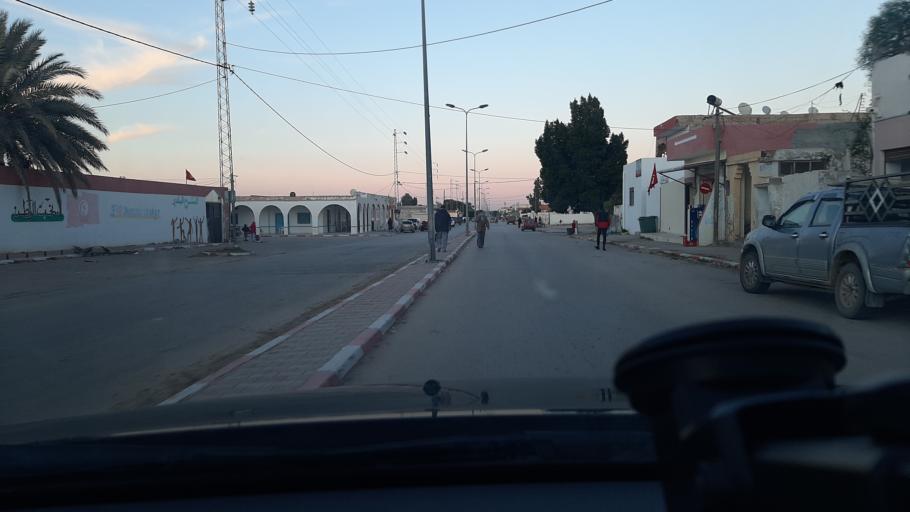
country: TN
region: Al Mahdiyah
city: Shurban
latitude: 34.9621
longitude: 10.3643
